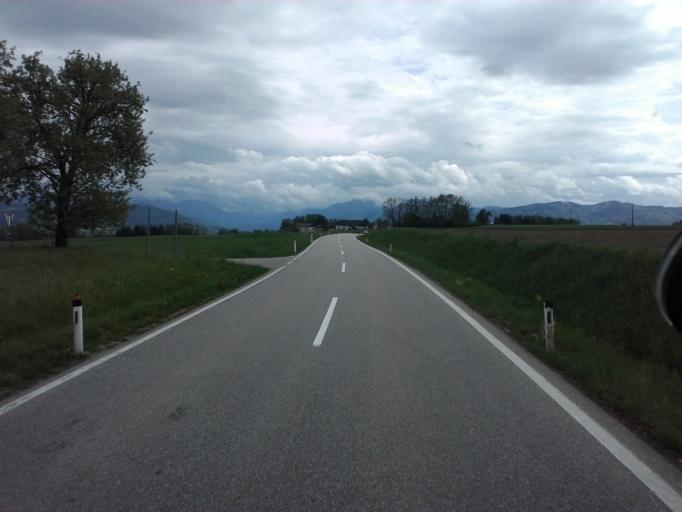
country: AT
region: Upper Austria
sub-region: Politischer Bezirk Kirchdorf an der Krems
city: Kremsmunster
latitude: 47.9902
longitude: 14.0790
